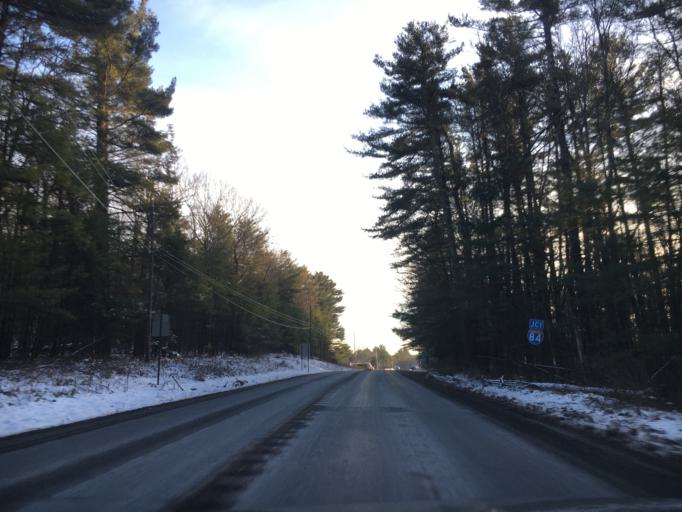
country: US
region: Pennsylvania
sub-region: Pike County
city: Hemlock Farms
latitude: 41.3699
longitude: -75.1275
